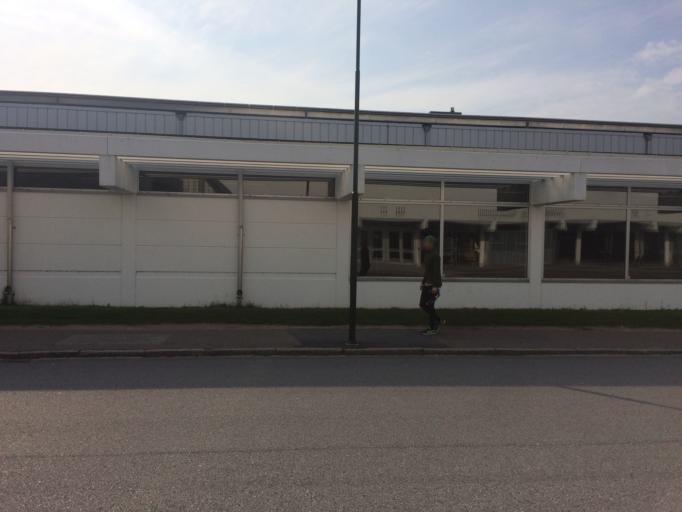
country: SE
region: Skane
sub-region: Malmo
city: Malmoe
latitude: 55.5836
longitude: 12.9905
